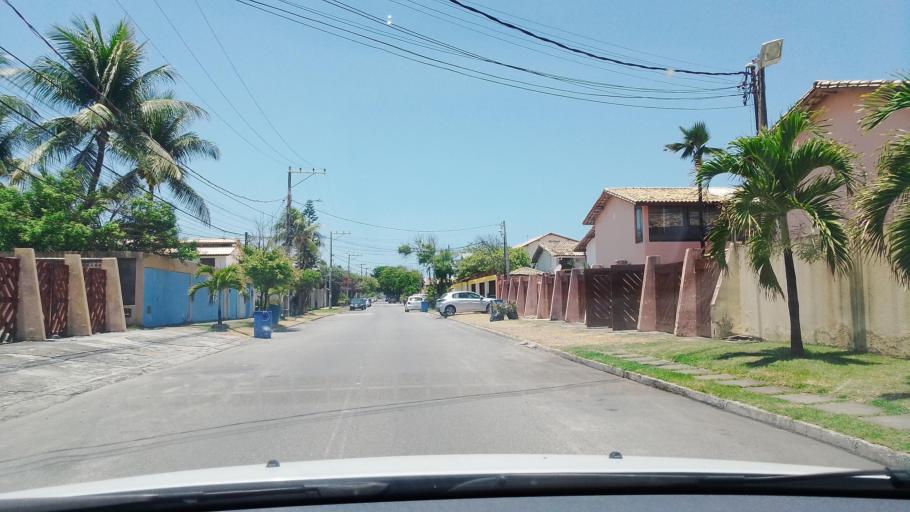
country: BR
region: Bahia
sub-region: Lauro De Freitas
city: Lauro de Freitas
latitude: -12.9417
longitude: -38.3336
